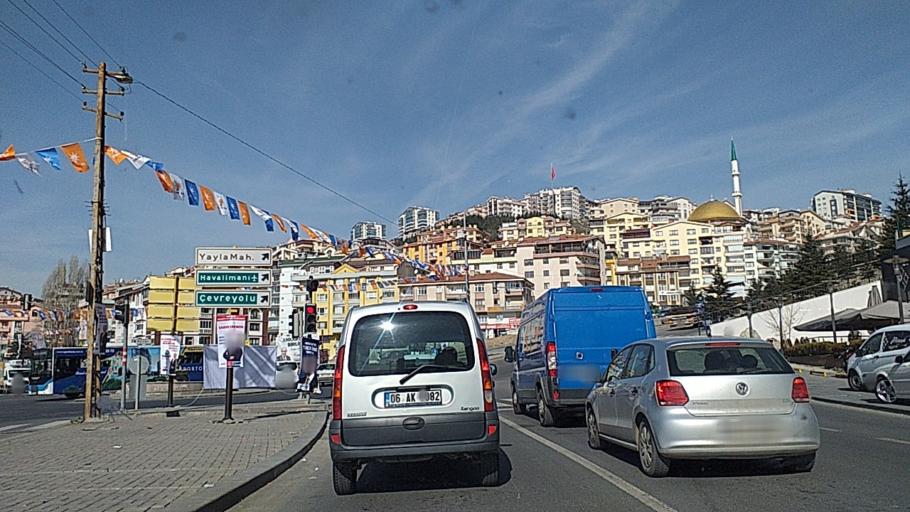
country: TR
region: Ankara
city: Ankara
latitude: 39.9880
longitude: 32.8205
